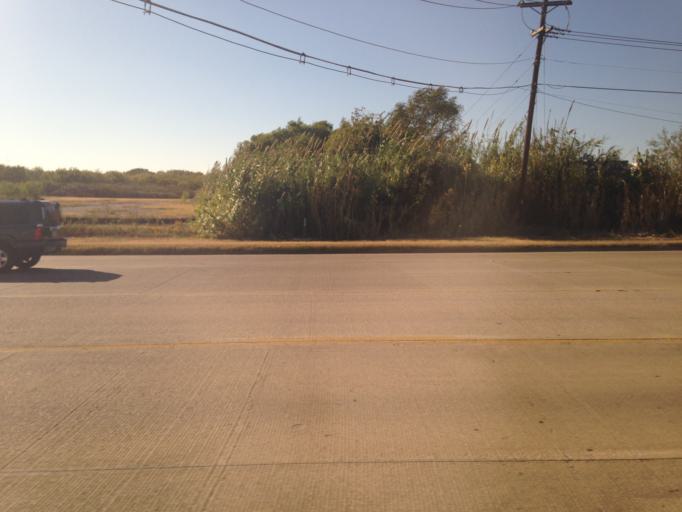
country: US
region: Texas
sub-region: Tarrant County
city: Watauga
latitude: 32.8445
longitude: -97.2640
